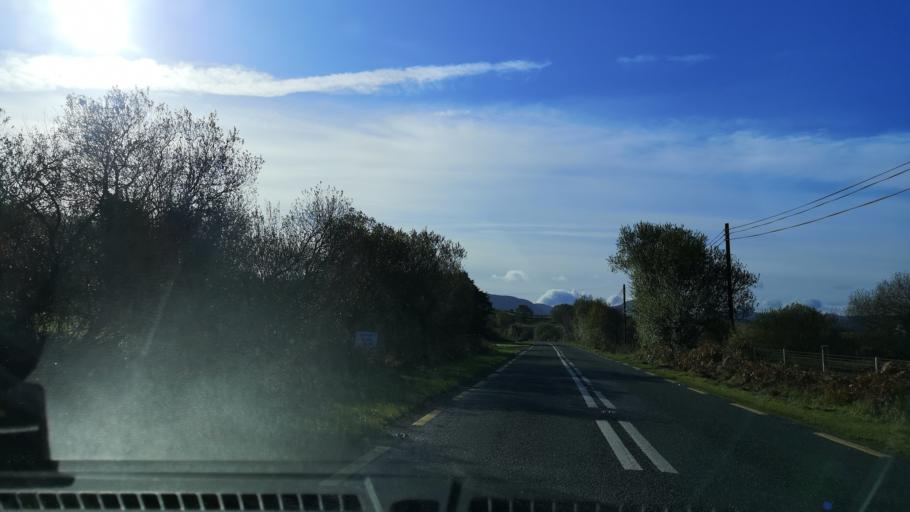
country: IE
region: Connaught
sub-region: Maigh Eo
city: Westport
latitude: 53.7079
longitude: -9.5631
